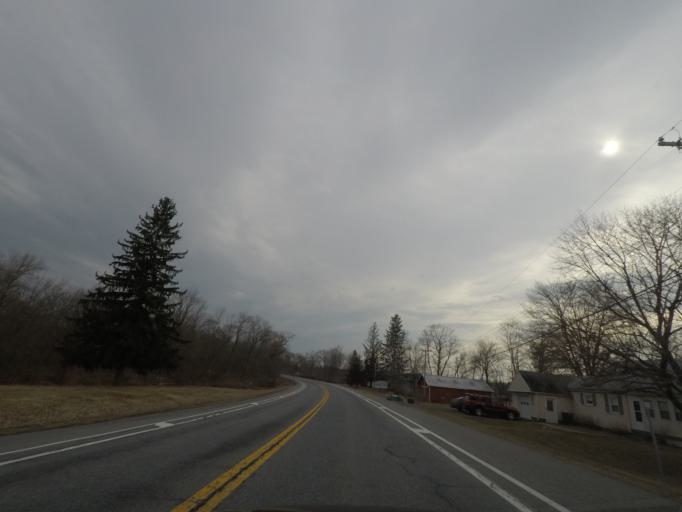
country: US
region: New York
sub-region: Washington County
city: Fort Edward
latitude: 43.2032
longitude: -73.5809
